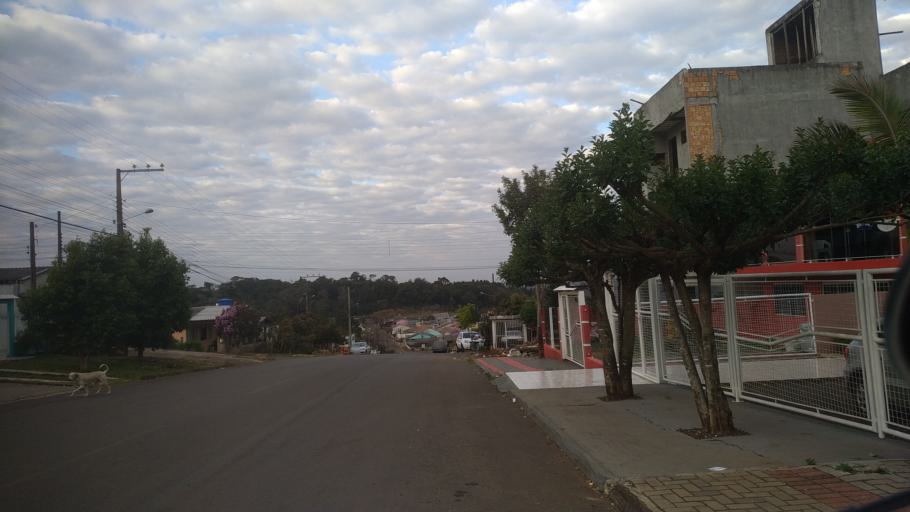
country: BR
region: Santa Catarina
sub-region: Chapeco
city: Chapeco
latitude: -27.1054
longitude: -52.6804
